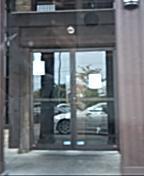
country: US
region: Kentucky
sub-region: Jefferson County
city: Douglass Hills
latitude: 38.2446
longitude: -85.5613
